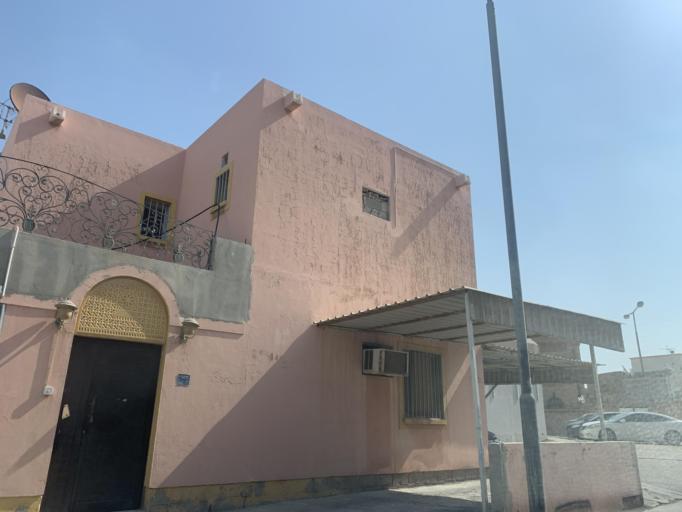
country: BH
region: Central Governorate
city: Madinat Hamad
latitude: 26.1317
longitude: 50.4989
